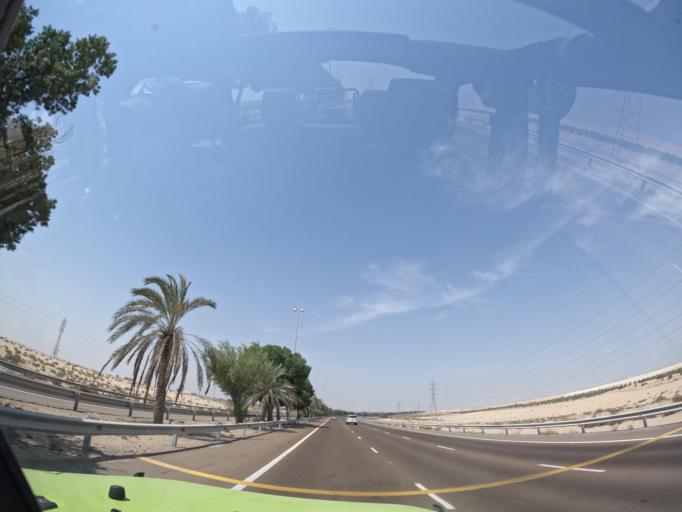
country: AE
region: Abu Dhabi
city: Abu Dhabi
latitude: 24.2326
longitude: 54.7653
